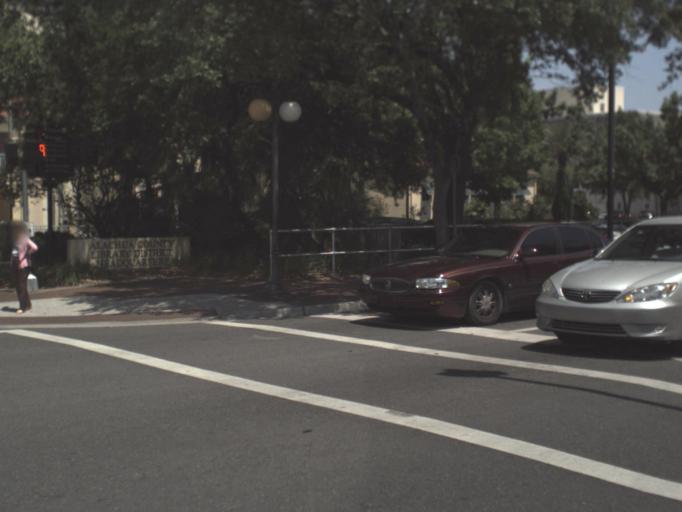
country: US
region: Florida
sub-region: Alachua County
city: Gainesville
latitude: 29.6519
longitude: -82.3225
